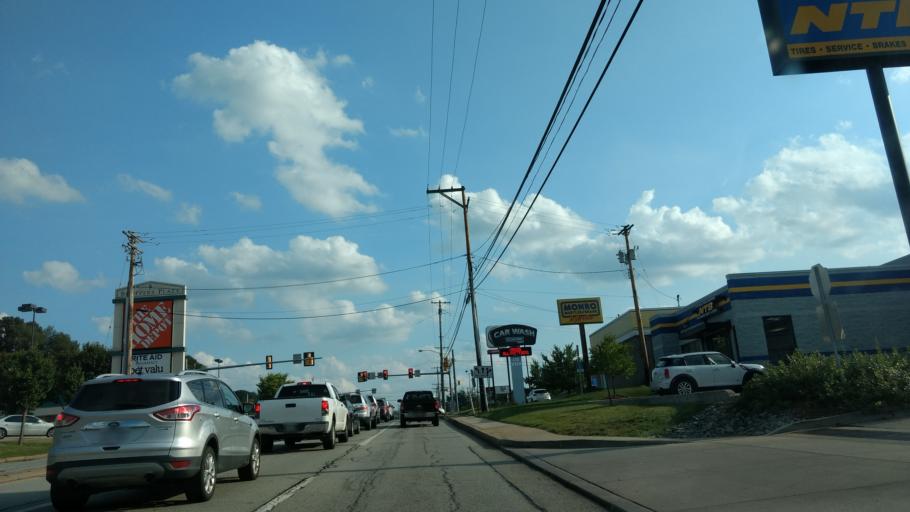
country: US
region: Pennsylvania
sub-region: Allegheny County
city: Gibsonia
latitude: 40.6031
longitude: -79.9473
